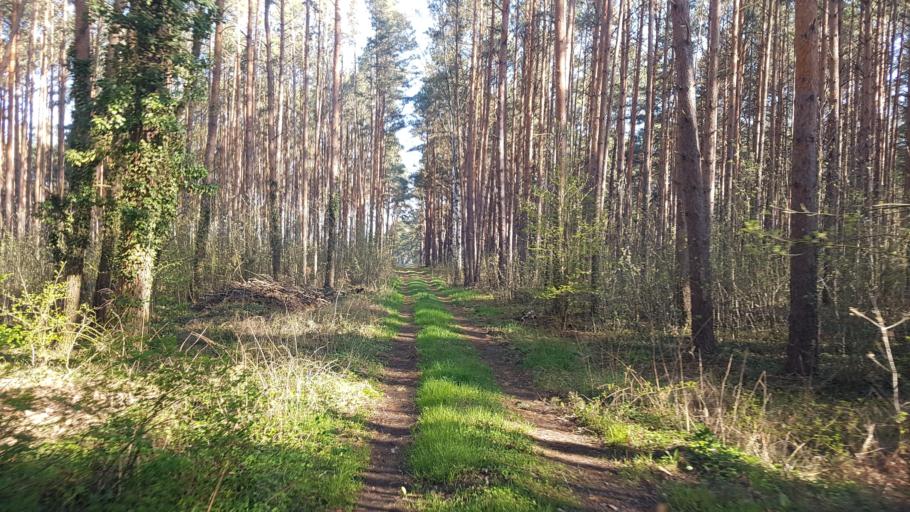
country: DE
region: Brandenburg
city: Bronkow
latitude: 51.6464
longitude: 13.8661
